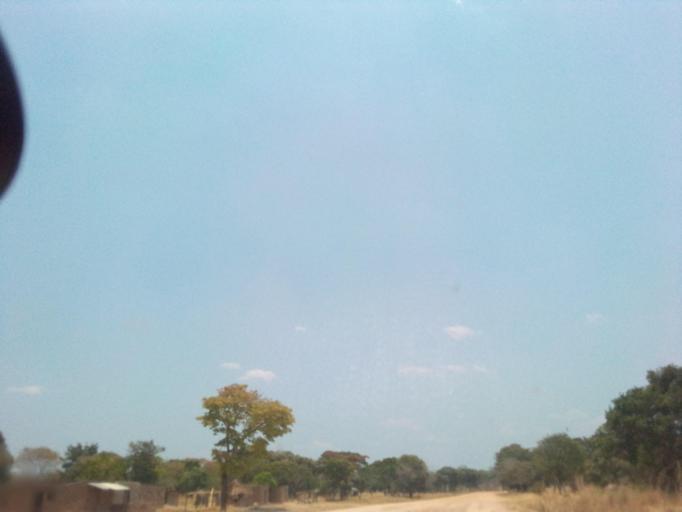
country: ZM
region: Northern
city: Chinsali
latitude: -10.8555
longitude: 31.6762
